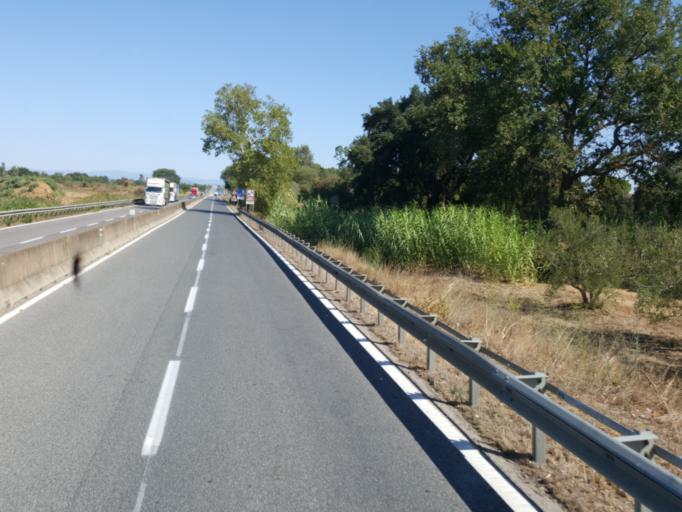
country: IT
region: Tuscany
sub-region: Provincia di Grosseto
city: Grosseto
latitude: 42.6701
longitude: 11.1423
